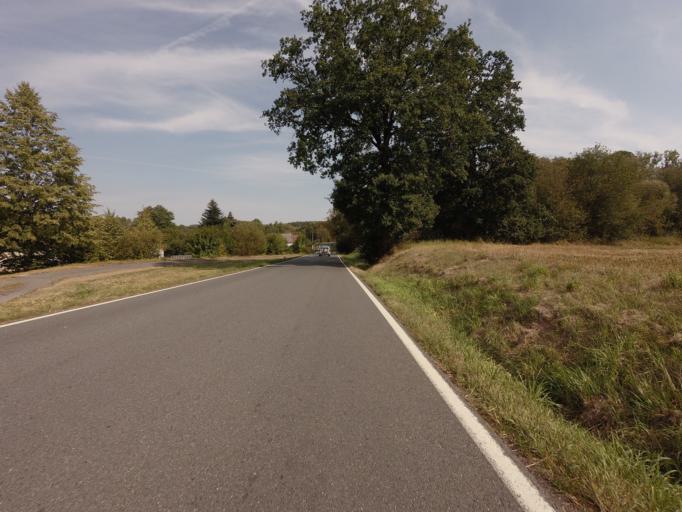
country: CZ
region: Central Bohemia
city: Petrovice
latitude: 49.5587
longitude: 14.3551
